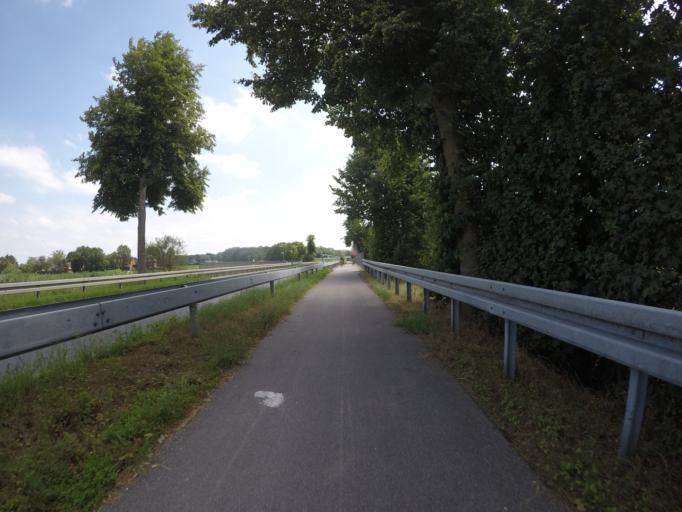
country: DE
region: North Rhine-Westphalia
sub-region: Regierungsbezirk Munster
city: Rhede
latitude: 51.8189
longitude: 6.7059
